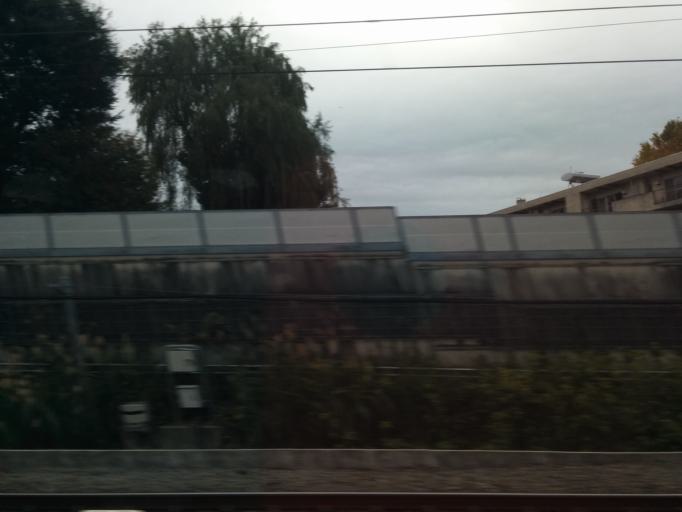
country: JP
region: Kanagawa
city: Odawara
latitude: 35.2540
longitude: 139.1529
